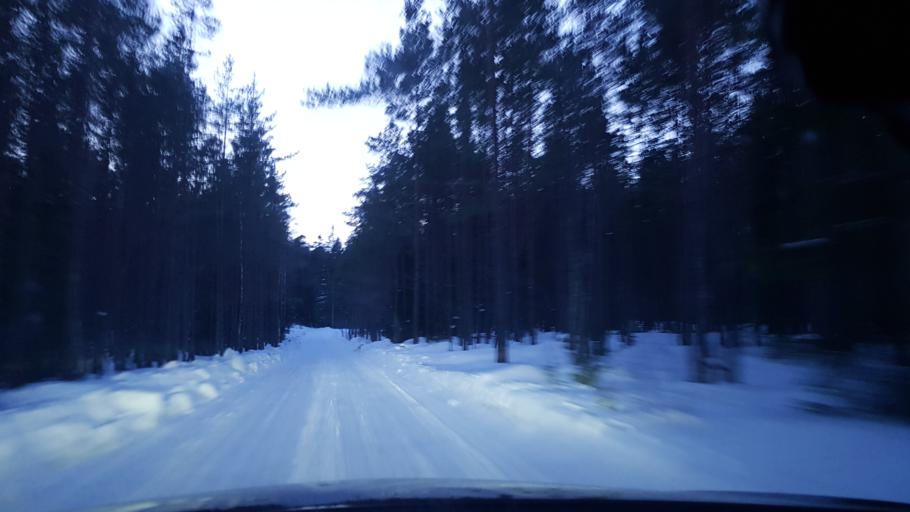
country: EE
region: Laeaene
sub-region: Haapsalu linn
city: Haapsalu
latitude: 59.2117
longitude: 23.5627
